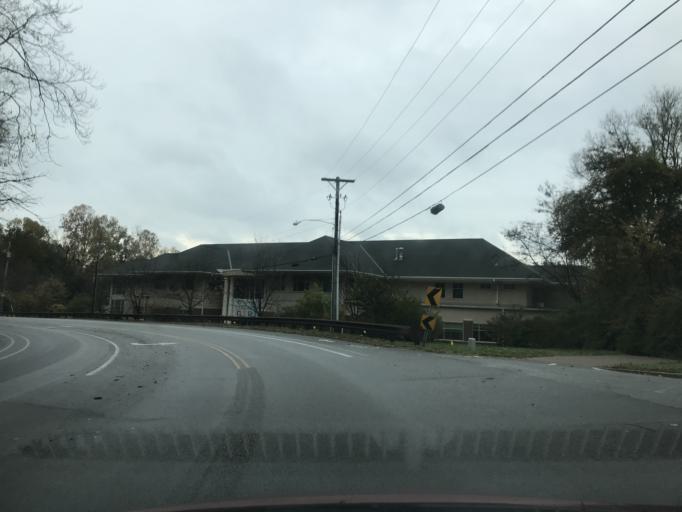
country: US
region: Indiana
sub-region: Clark County
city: Jeffersonville
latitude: 38.2474
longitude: -85.7076
